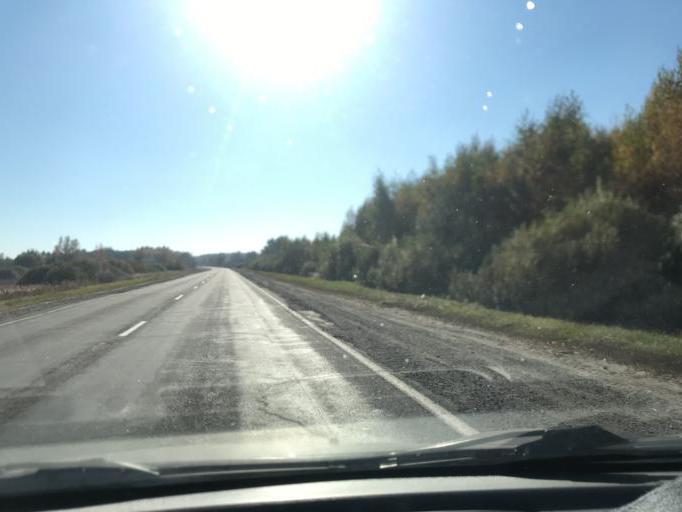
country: BY
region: Gomel
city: Kastsyukowka
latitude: 52.4476
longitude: 30.8250
